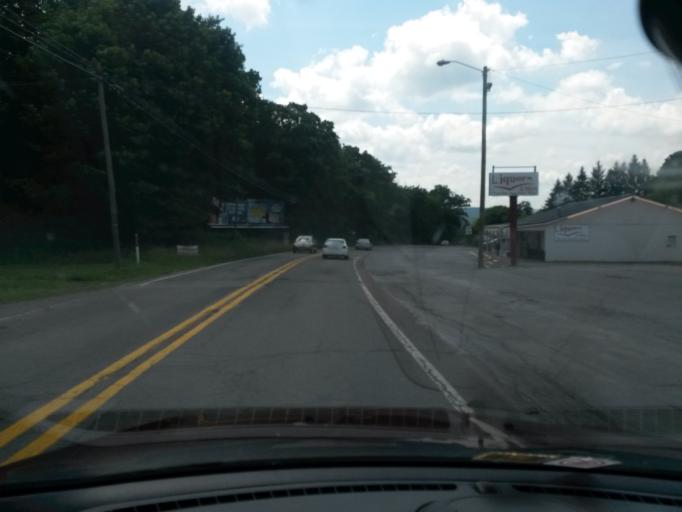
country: US
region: West Virginia
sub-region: Mercer County
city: Princeton
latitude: 37.3710
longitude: -81.1105
